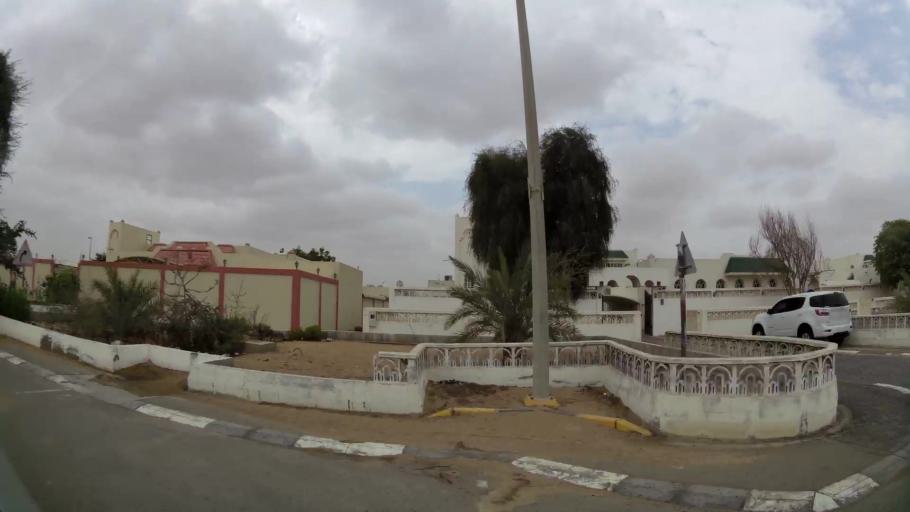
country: AE
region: Abu Dhabi
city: Abu Dhabi
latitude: 24.3285
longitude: 54.6370
